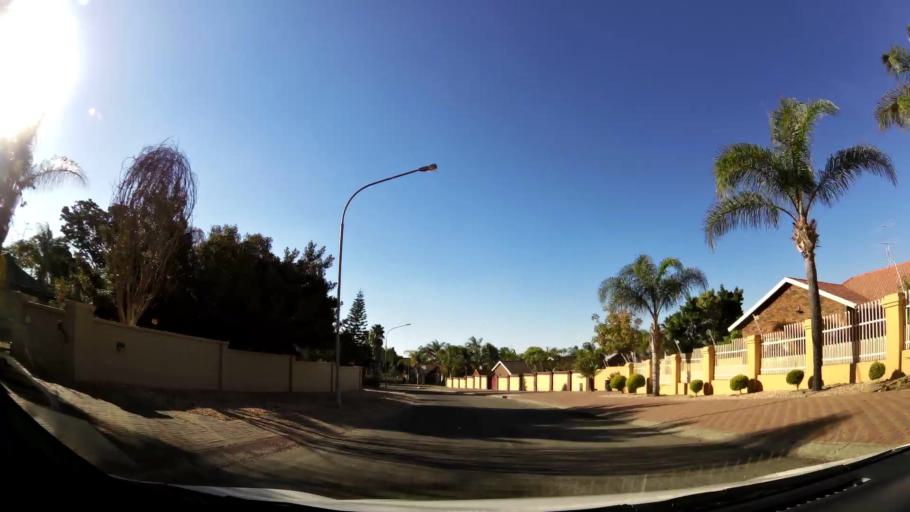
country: ZA
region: Limpopo
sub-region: Capricorn District Municipality
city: Polokwane
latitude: -23.8843
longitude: 29.4890
